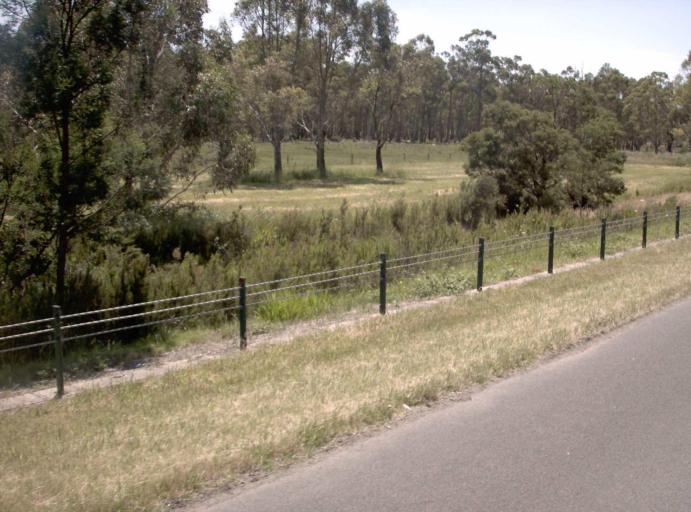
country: AU
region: Victoria
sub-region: Cardinia
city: Pakenham Upper
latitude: -38.0698
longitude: 145.5815
